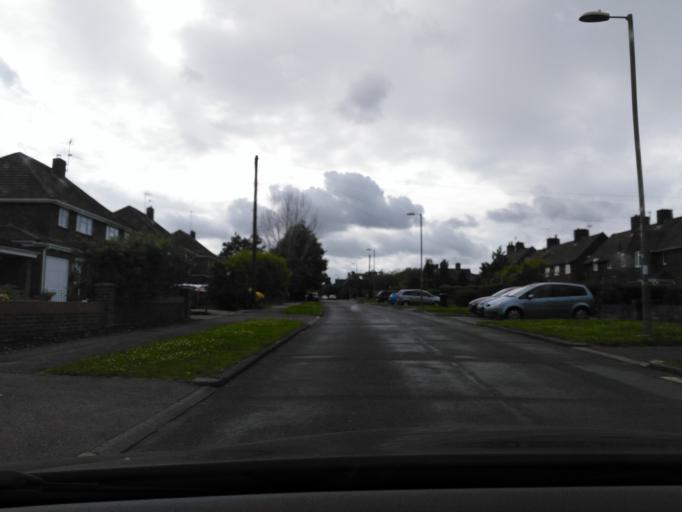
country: GB
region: England
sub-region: Hampshire
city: Basingstoke
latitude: 51.2726
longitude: -1.0788
